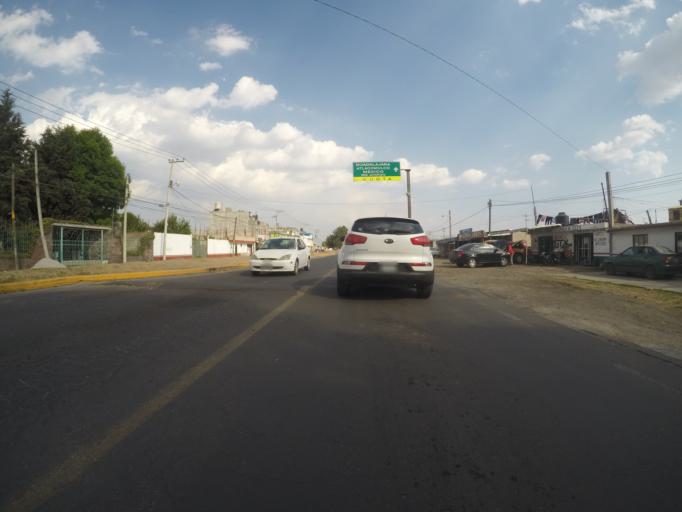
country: MX
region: Morelos
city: Chapultepec
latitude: 19.2018
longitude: -99.5492
